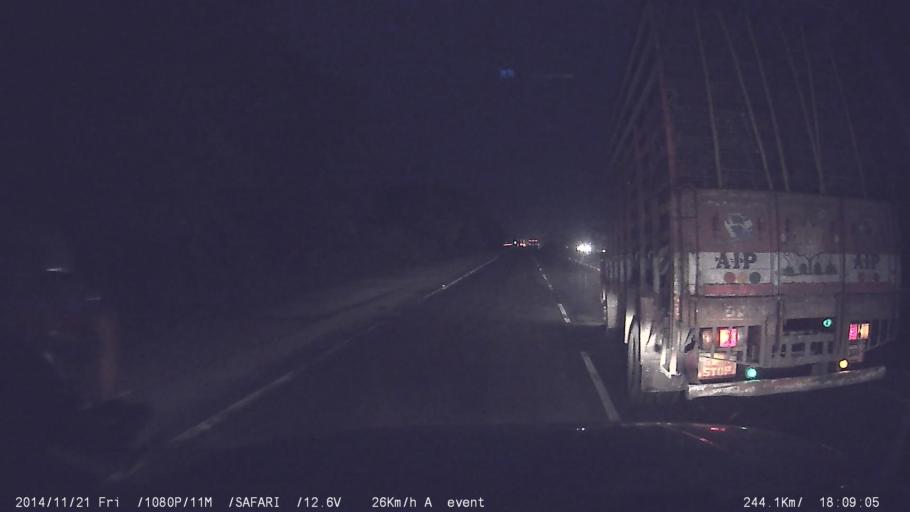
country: IN
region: Tamil Nadu
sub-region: Vellore
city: Walajapet
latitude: 12.8980
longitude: 79.5343
